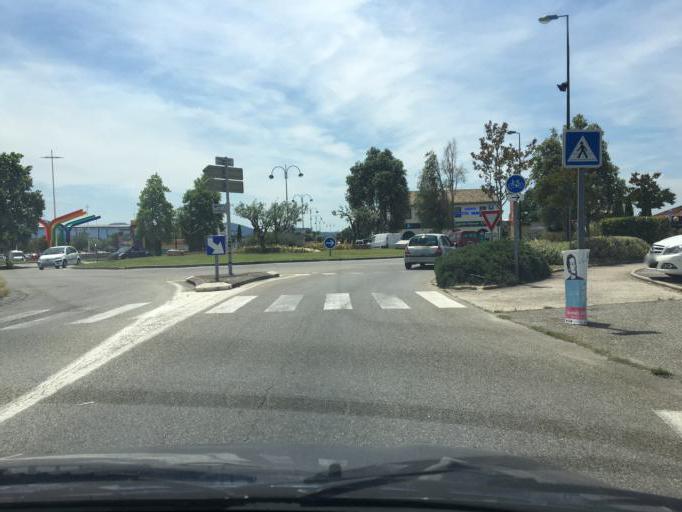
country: FR
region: Rhone-Alpes
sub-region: Departement de la Drome
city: Montelimar
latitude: 44.5339
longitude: 4.7460
